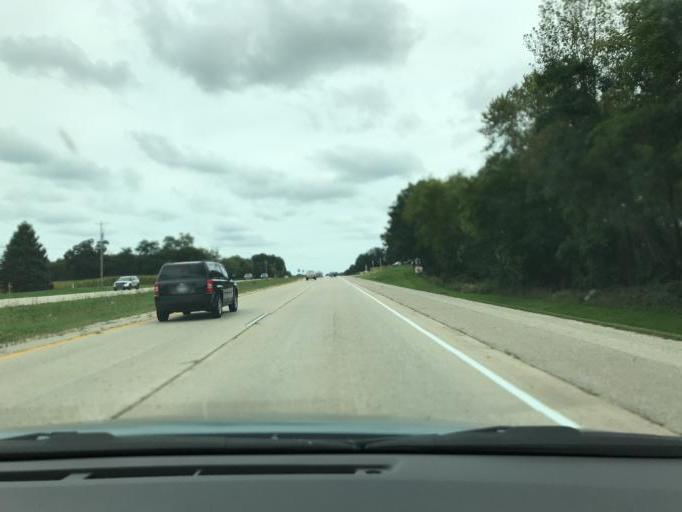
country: US
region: Wisconsin
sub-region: Kenosha County
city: Paddock Lake
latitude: 42.5680
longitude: -88.0800
